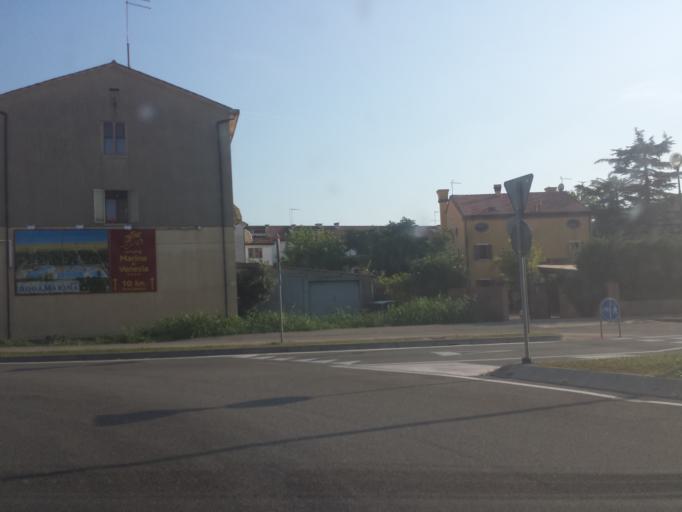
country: IT
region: Veneto
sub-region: Provincia di Venezia
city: Cavallino
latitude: 45.4815
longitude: 12.5500
